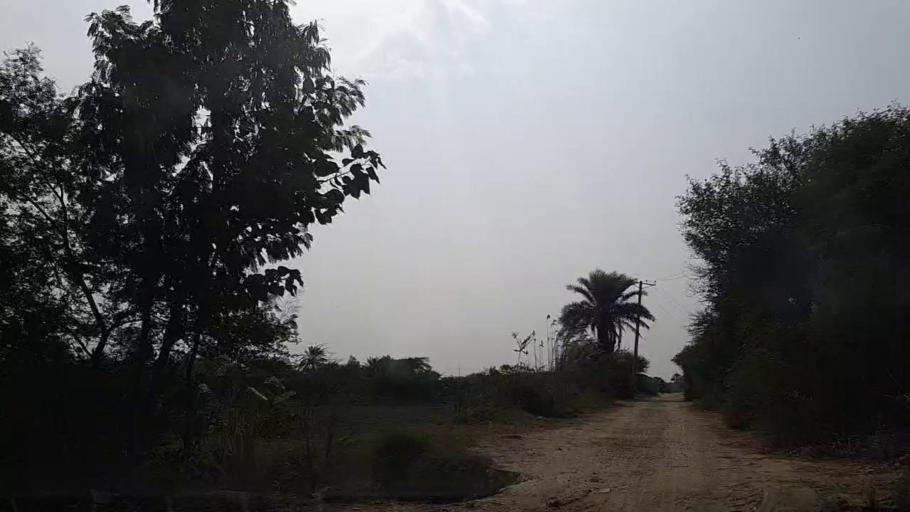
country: PK
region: Sindh
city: Mirpur Sakro
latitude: 24.6202
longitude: 67.7438
